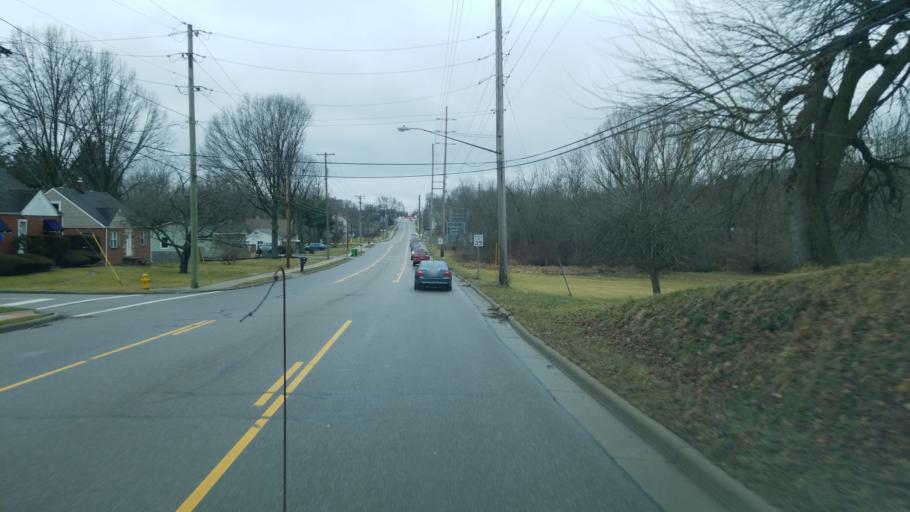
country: US
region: Ohio
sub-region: Summit County
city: Norton
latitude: 41.0119
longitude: -81.6386
